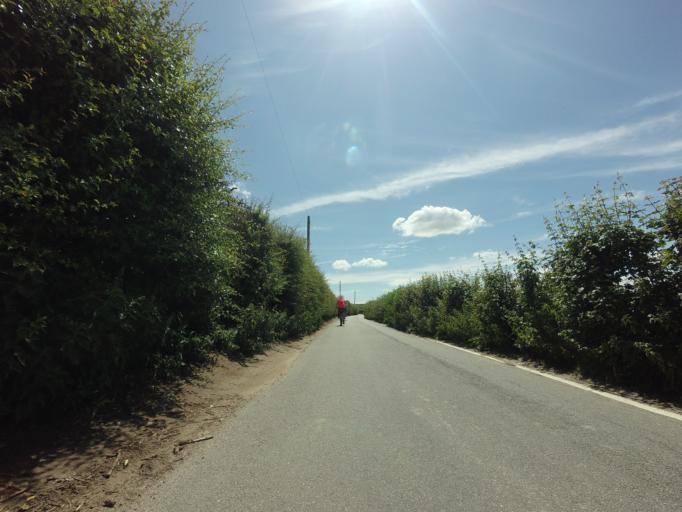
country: GB
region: England
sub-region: Medway
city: Cooling
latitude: 51.4557
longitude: 0.5399
